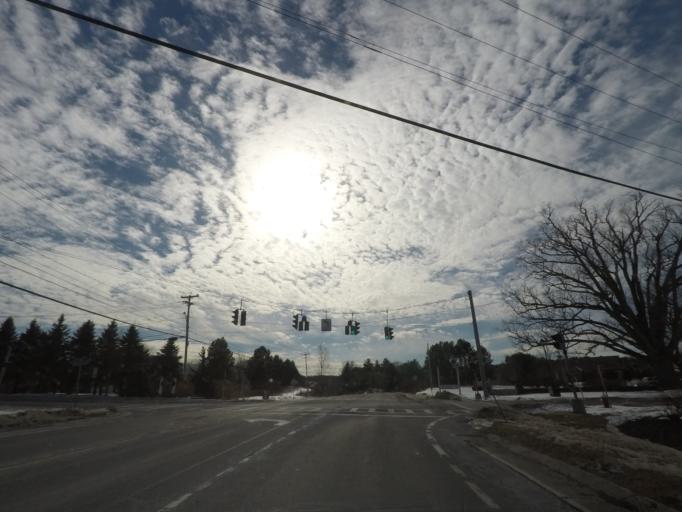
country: US
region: New York
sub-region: Albany County
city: Westmere
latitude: 42.6829
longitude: -73.9028
